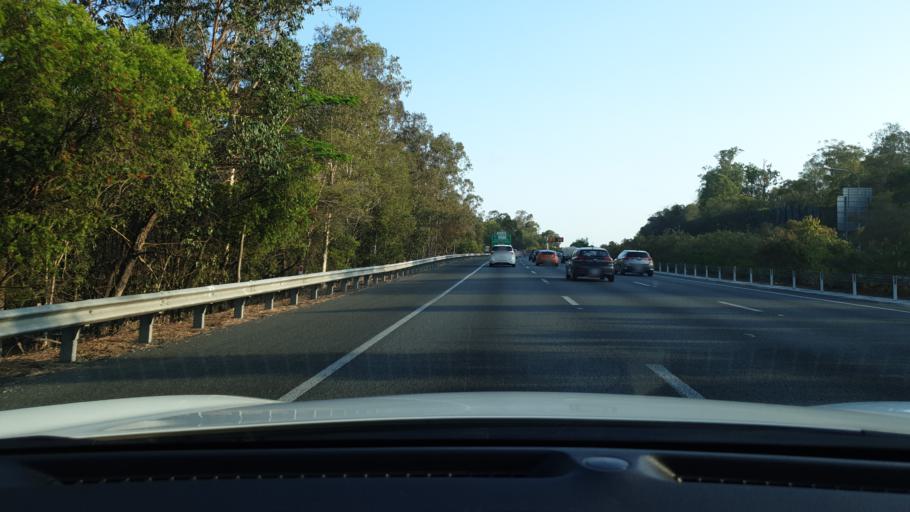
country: AU
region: Queensland
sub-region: Gold Coast
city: Nerang
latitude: -27.9658
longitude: 153.3464
